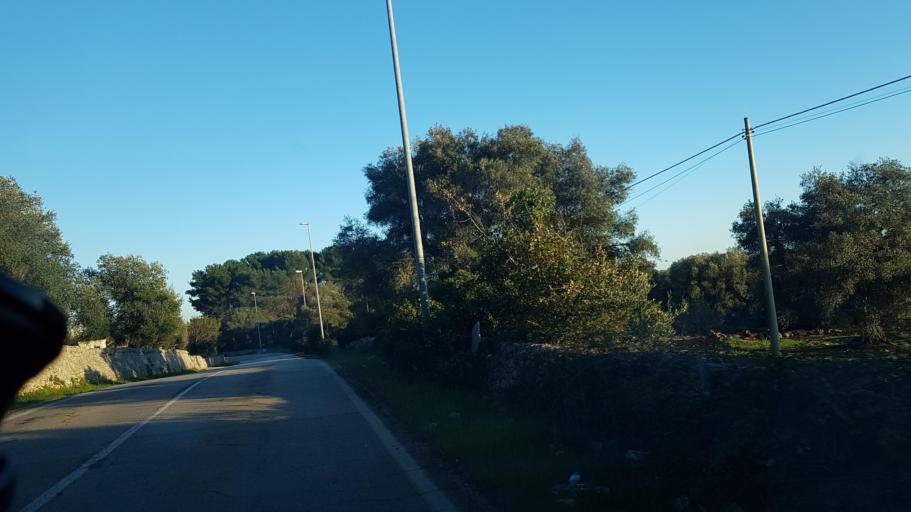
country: IT
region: Apulia
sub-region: Provincia di Brindisi
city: Ostuni
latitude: 40.7076
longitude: 17.5382
